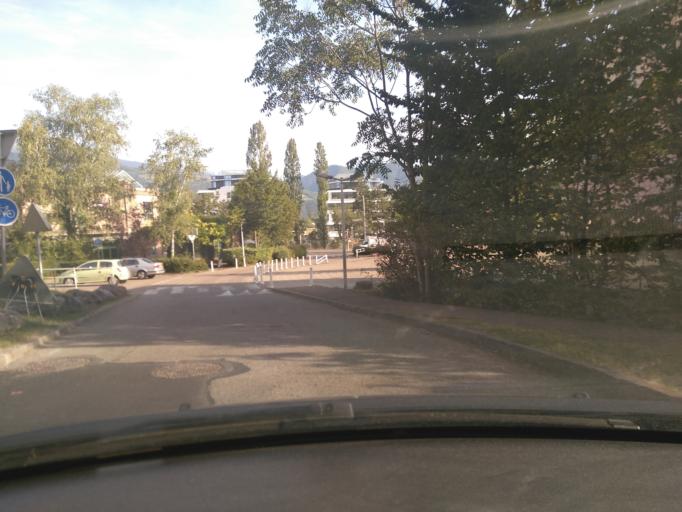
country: FR
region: Rhone-Alpes
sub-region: Departement de l'Isere
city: Meylan
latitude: 45.2121
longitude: 5.7866
